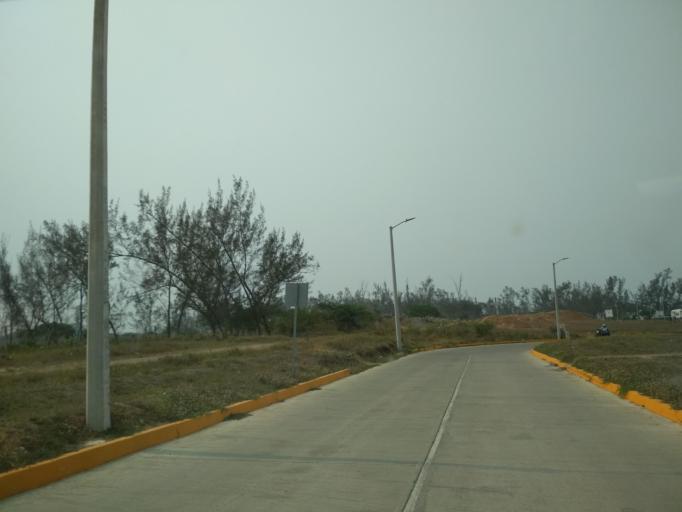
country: MX
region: Veracruz
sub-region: Veracruz
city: Las Amapolas
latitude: 19.1437
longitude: -96.2240
